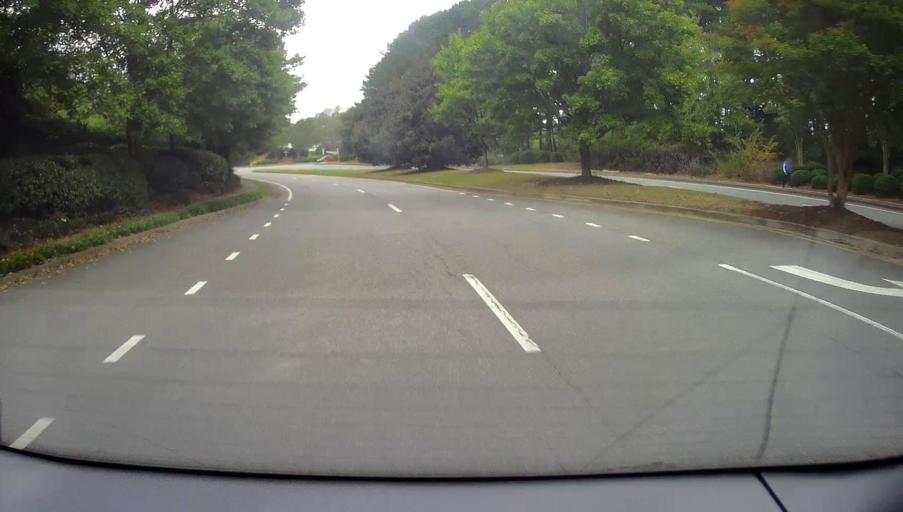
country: US
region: Georgia
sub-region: Fulton County
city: Alpharetta
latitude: 34.1047
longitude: -84.2654
